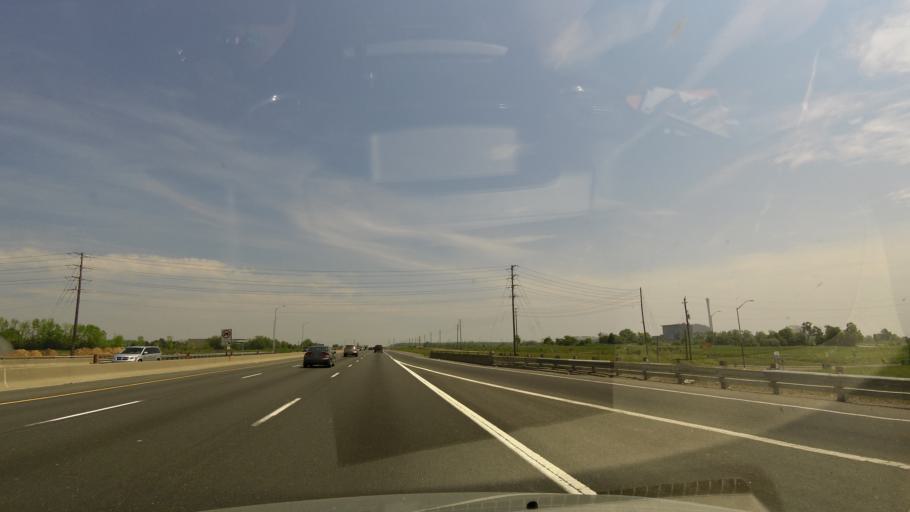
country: CA
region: Ontario
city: Oshawa
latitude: 43.8785
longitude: -78.7642
